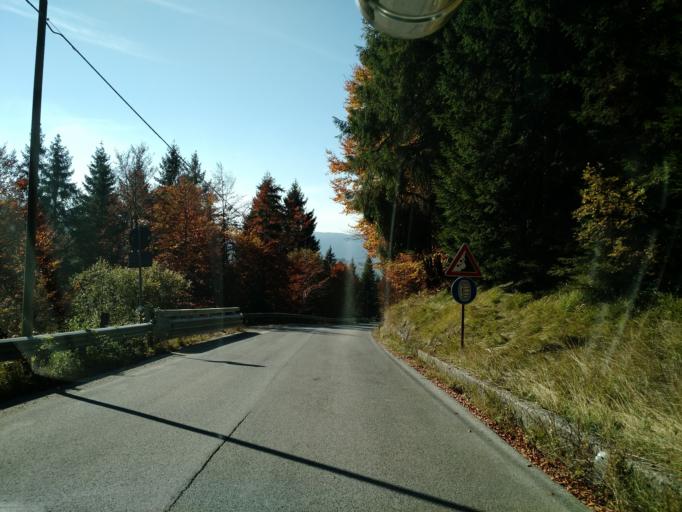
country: IT
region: Veneto
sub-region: Provincia di Vicenza
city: Gallio
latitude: 45.9070
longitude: 11.5683
